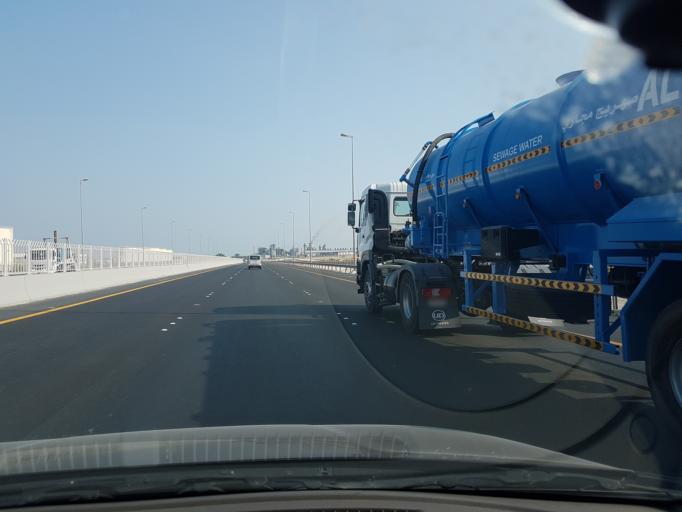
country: BH
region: Northern
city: Ar Rifa'
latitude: 26.1056
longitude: 50.6007
